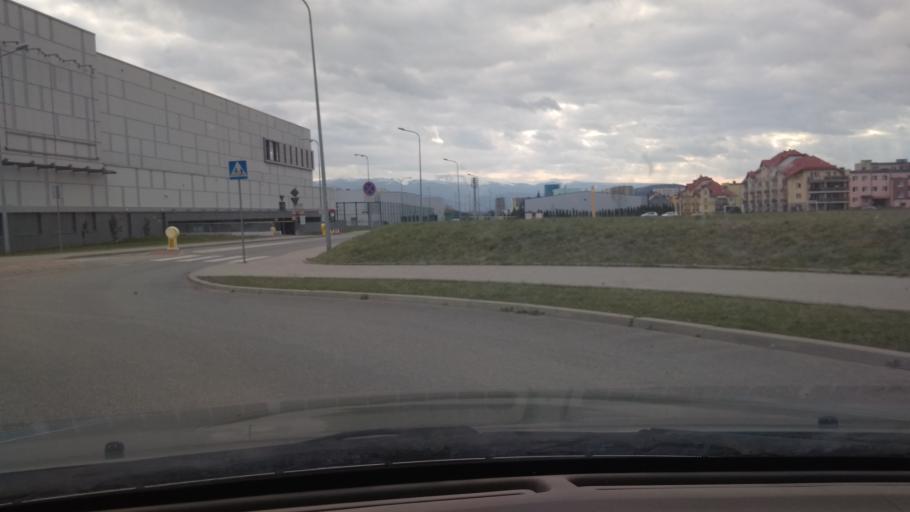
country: PL
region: Lower Silesian Voivodeship
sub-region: Powiat jeleniogorski
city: Jezow Sudecki
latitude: 50.9240
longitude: 15.7630
